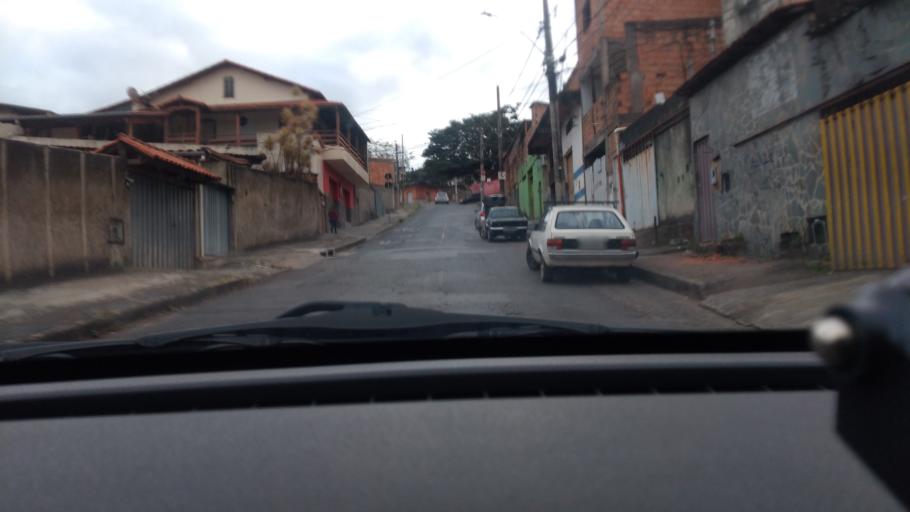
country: BR
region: Minas Gerais
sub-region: Belo Horizonte
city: Belo Horizonte
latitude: -19.8400
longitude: -43.9261
